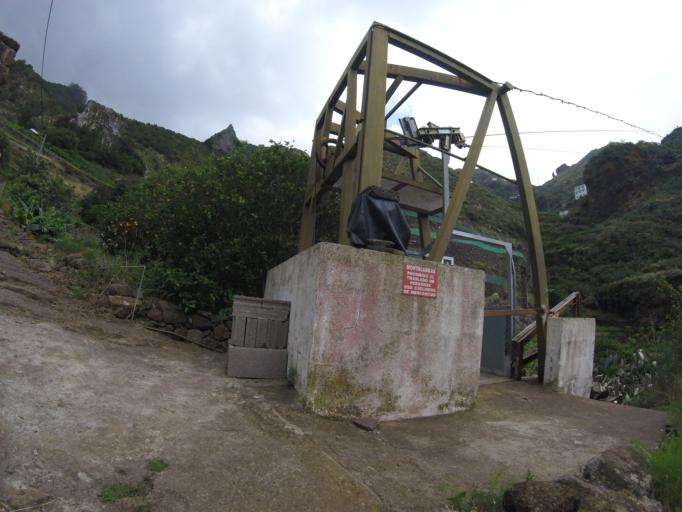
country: ES
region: Canary Islands
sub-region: Provincia de Santa Cruz de Tenerife
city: Tegueste
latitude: 28.5469
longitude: -16.2942
